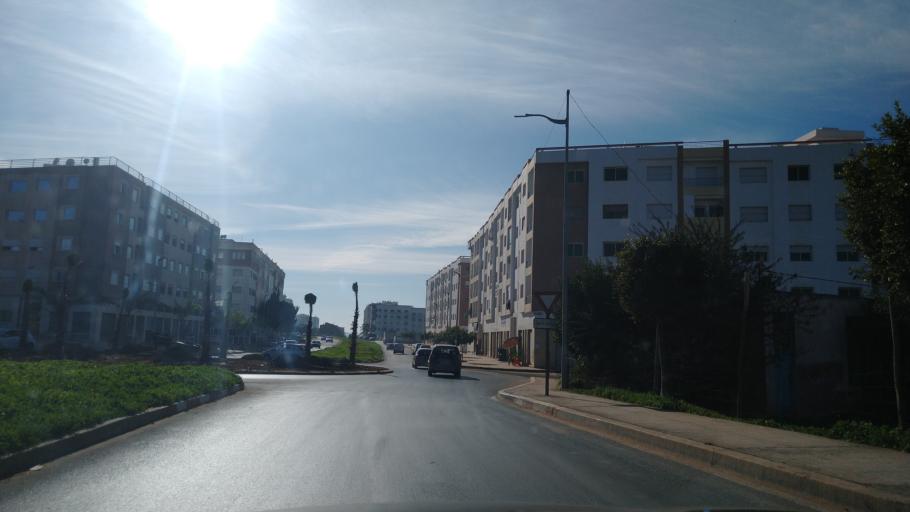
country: MA
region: Rabat-Sale-Zemmour-Zaer
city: Sale
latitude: 34.0070
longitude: -6.7429
